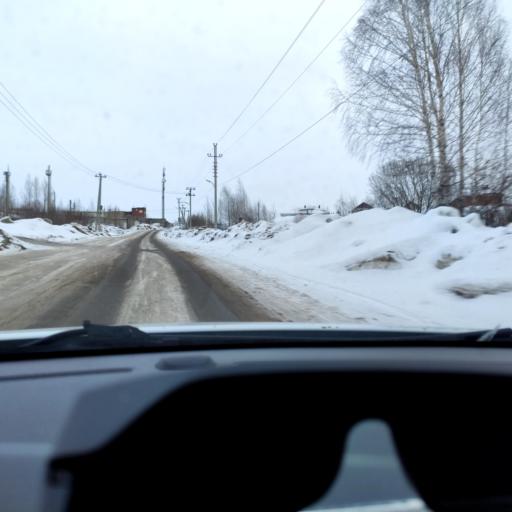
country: RU
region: Tatarstan
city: Vysokaya Gora
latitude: 55.8577
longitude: 49.2486
